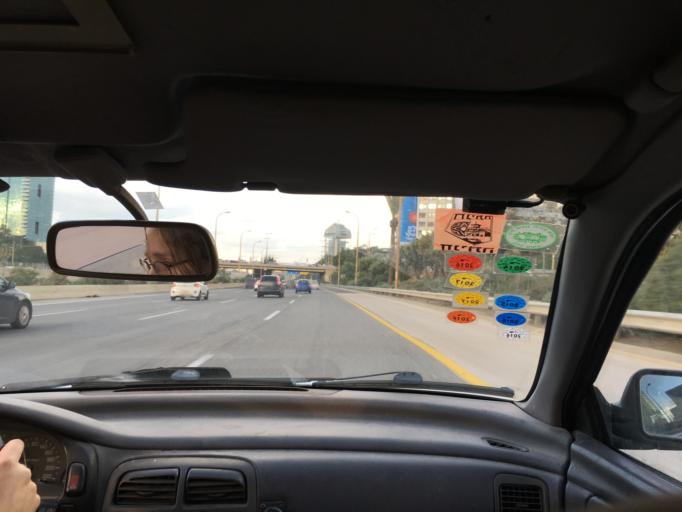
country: IL
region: Tel Aviv
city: Ramat Gan
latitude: 32.0875
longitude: 34.8004
